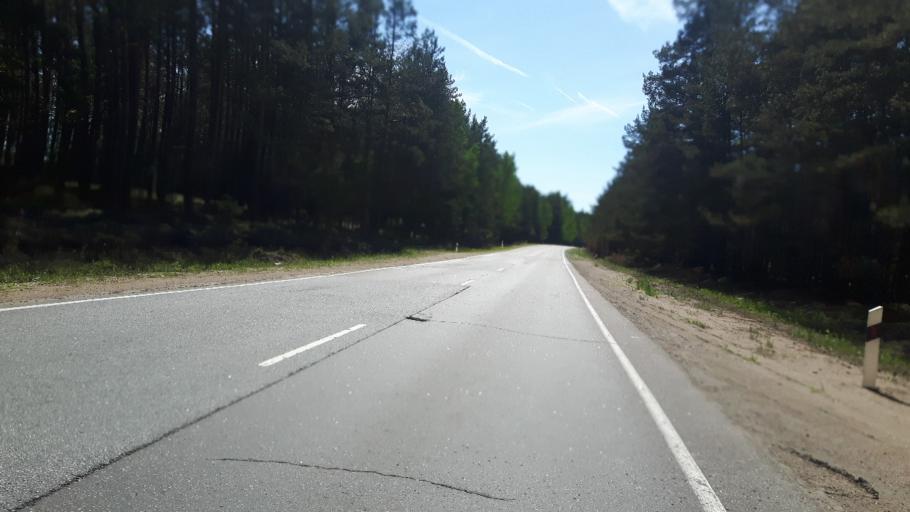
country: RU
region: Leningrad
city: Sista-Palkino
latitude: 59.7778
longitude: 28.8647
